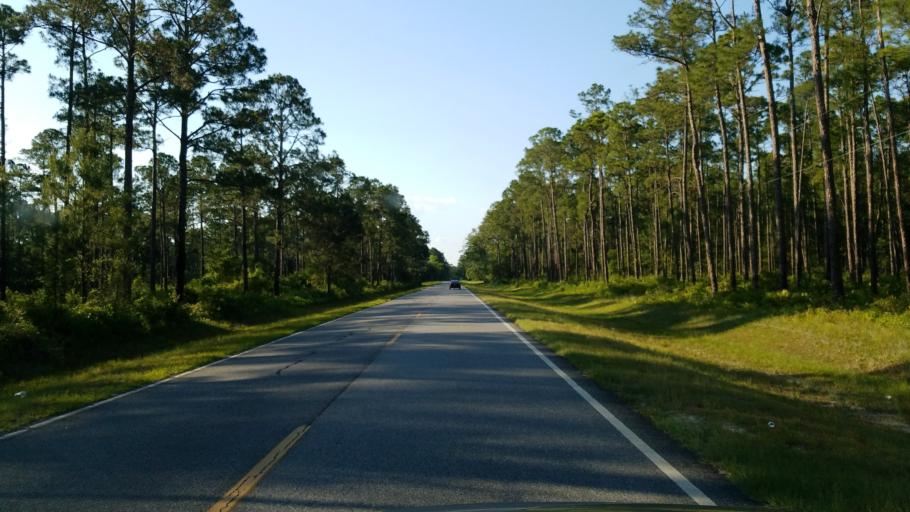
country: US
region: Georgia
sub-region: Lanier County
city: Lakeland
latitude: 30.9416
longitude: -83.0814
